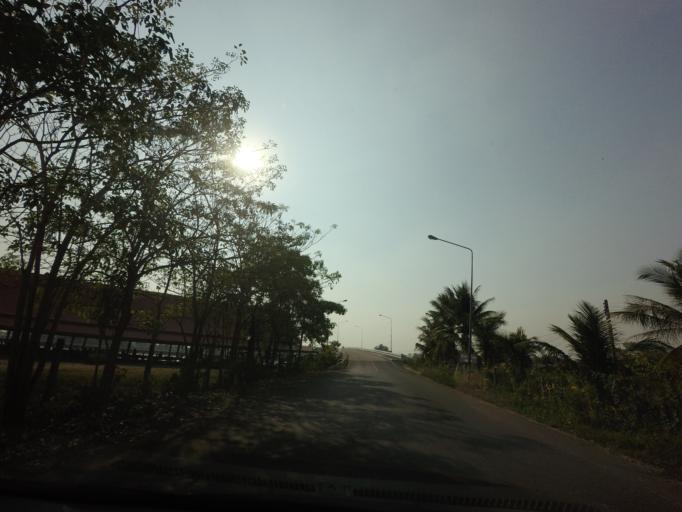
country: TH
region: Chachoengsao
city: Khlong Khuean
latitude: 13.8154
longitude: 101.1813
